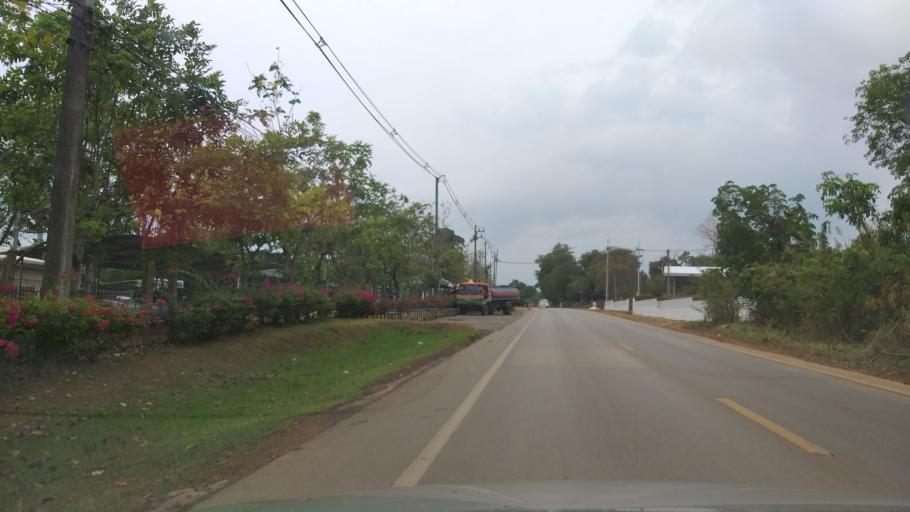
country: TH
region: Trat
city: Laem Ngop
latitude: 12.1904
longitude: 102.2953
